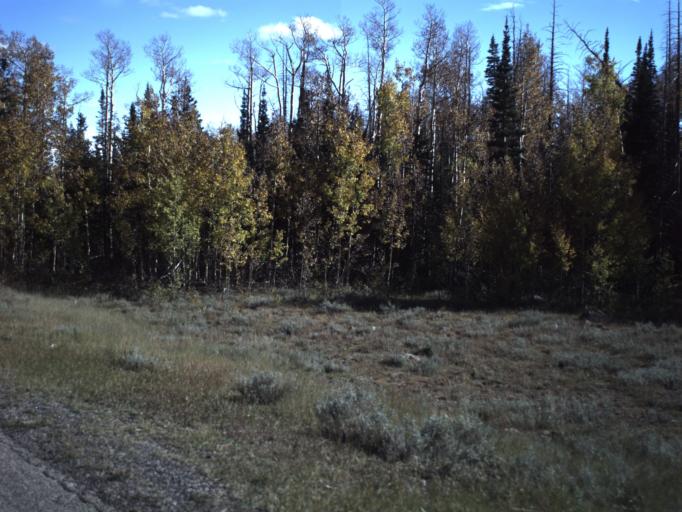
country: US
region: Utah
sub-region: Iron County
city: Parowan
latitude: 37.6547
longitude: -112.7587
